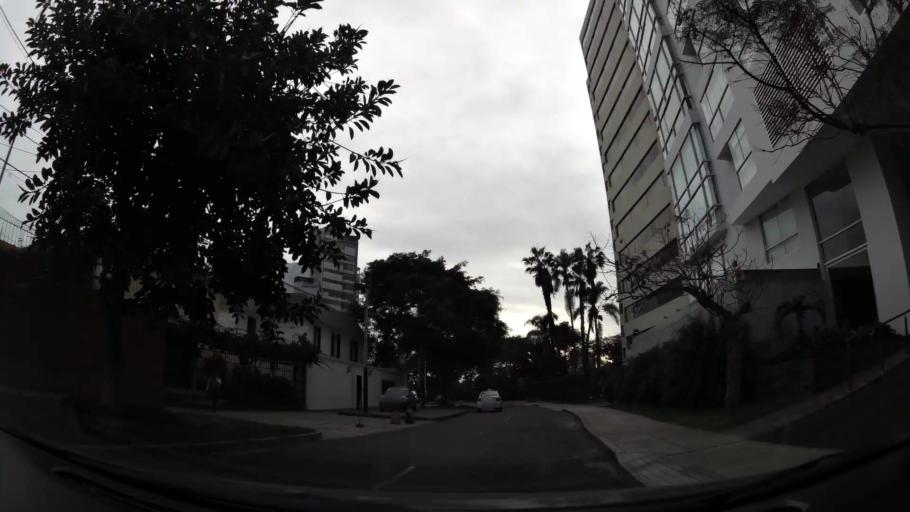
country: PE
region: Lima
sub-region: Lima
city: San Isidro
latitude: -12.1031
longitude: -77.0458
